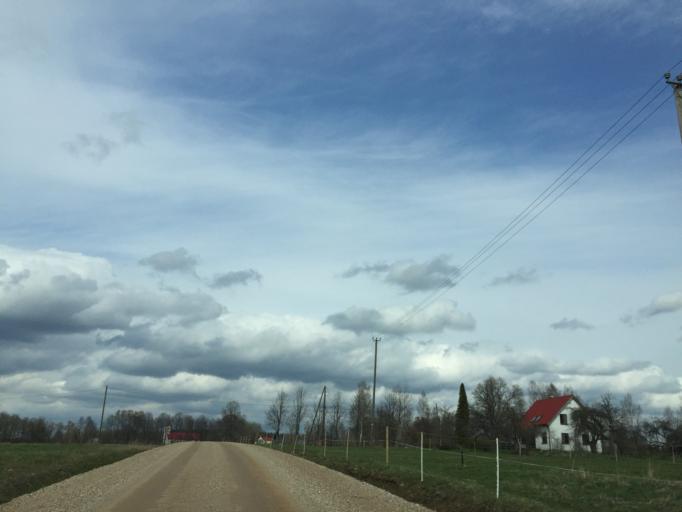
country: LV
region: Ligatne
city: Ligatne
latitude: 57.2124
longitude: 25.0673
